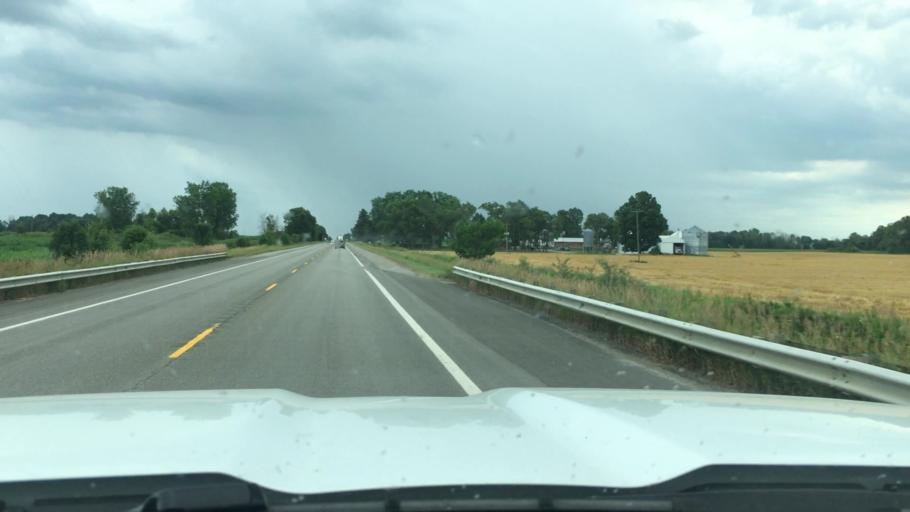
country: US
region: Michigan
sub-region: Montcalm County
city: Carson City
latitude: 43.1766
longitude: -84.8077
